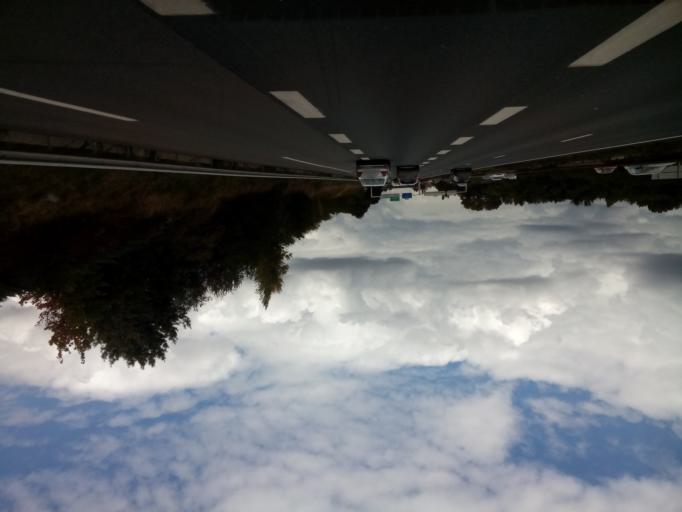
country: FR
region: Rhone-Alpes
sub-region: Departement du Rhone
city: Dardilly
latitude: 45.8137
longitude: 4.7668
